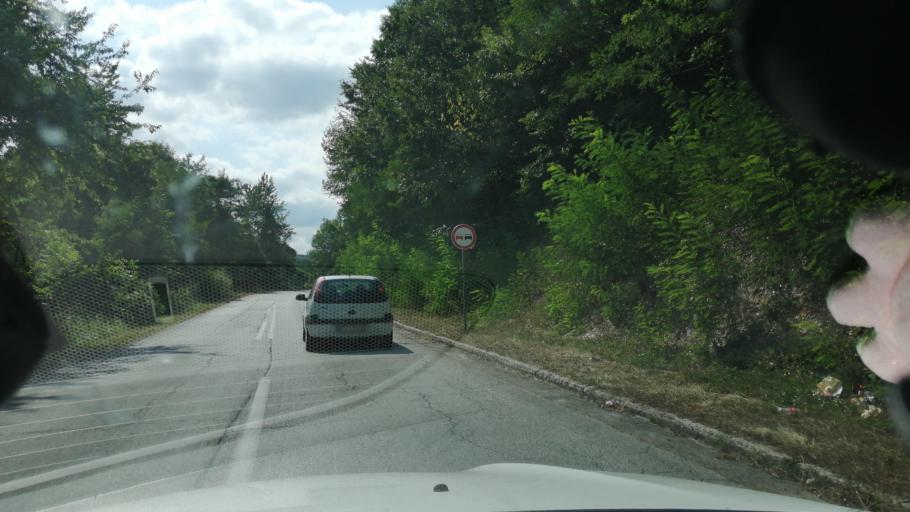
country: RS
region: Central Serbia
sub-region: Moravicki Okrug
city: Ivanjica
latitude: 43.6653
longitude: 20.2645
